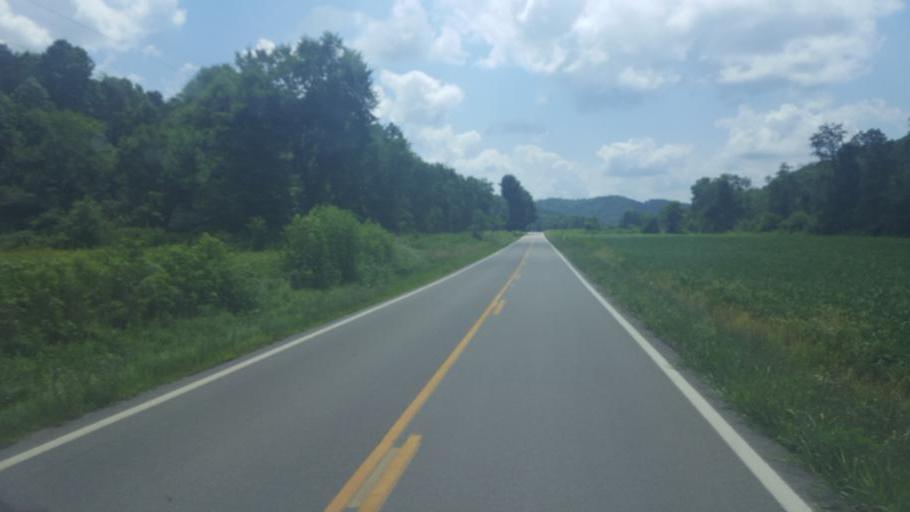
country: US
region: Ohio
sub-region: Ross County
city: Kingston
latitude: 39.3640
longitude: -82.7266
